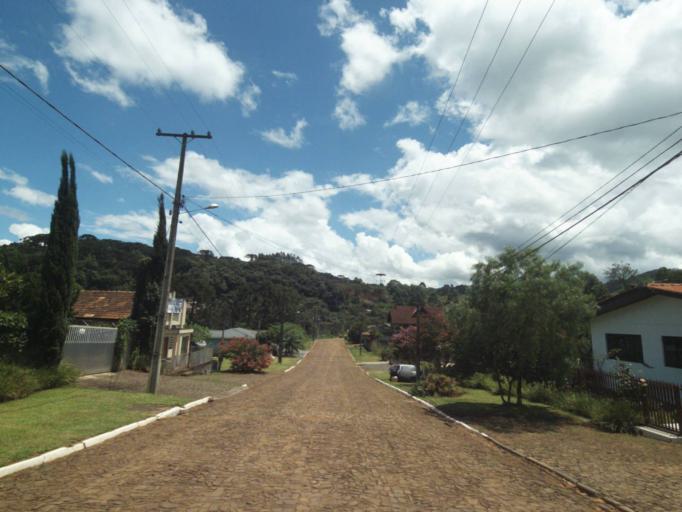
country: BR
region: Parana
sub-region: Uniao Da Vitoria
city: Uniao da Vitoria
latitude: -26.1664
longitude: -51.5572
